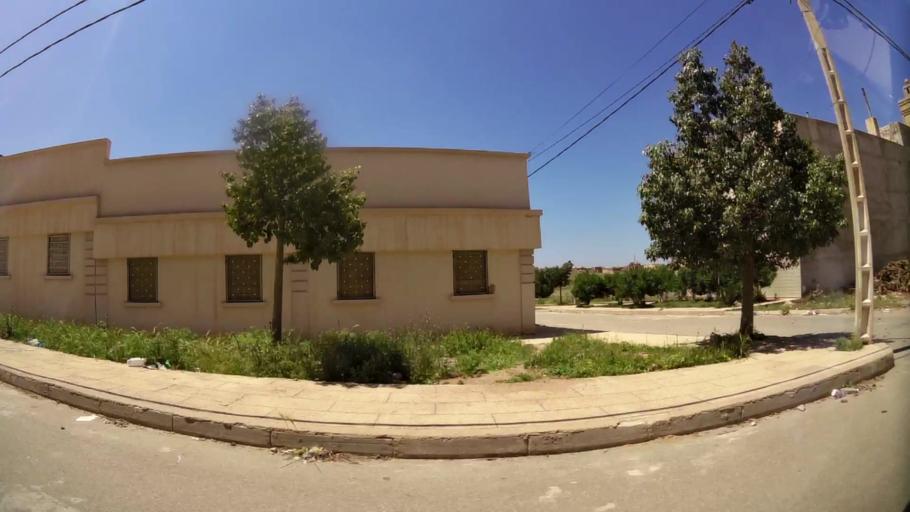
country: MA
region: Oriental
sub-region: Oujda-Angad
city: Oujda
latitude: 34.6848
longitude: -1.9494
